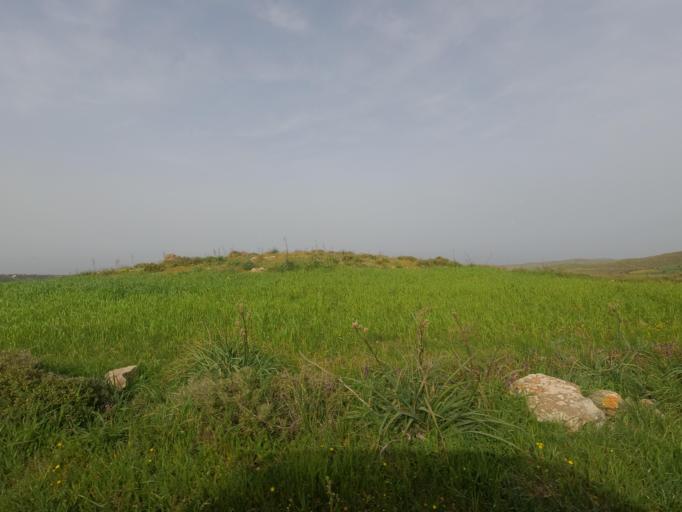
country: CY
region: Pafos
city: Pegeia
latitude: 34.9531
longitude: 32.3787
